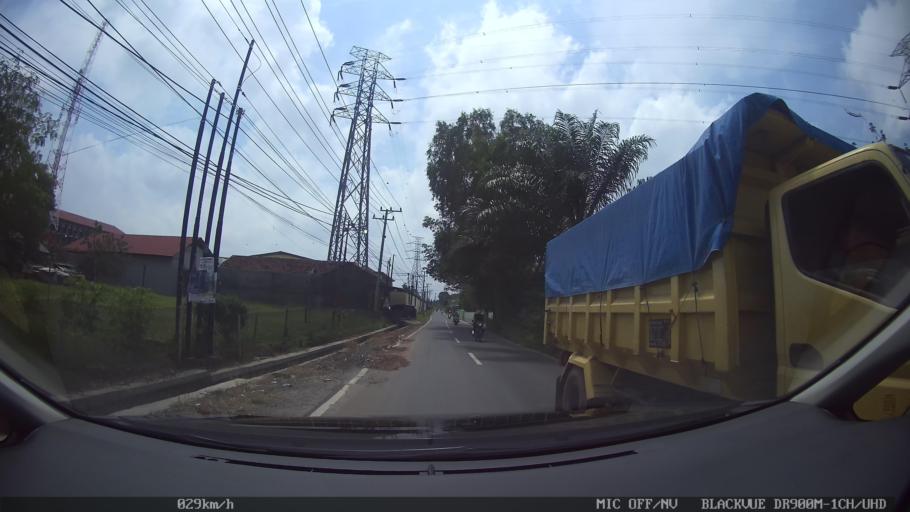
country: ID
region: Lampung
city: Kedaton
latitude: -5.3611
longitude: 105.3058
